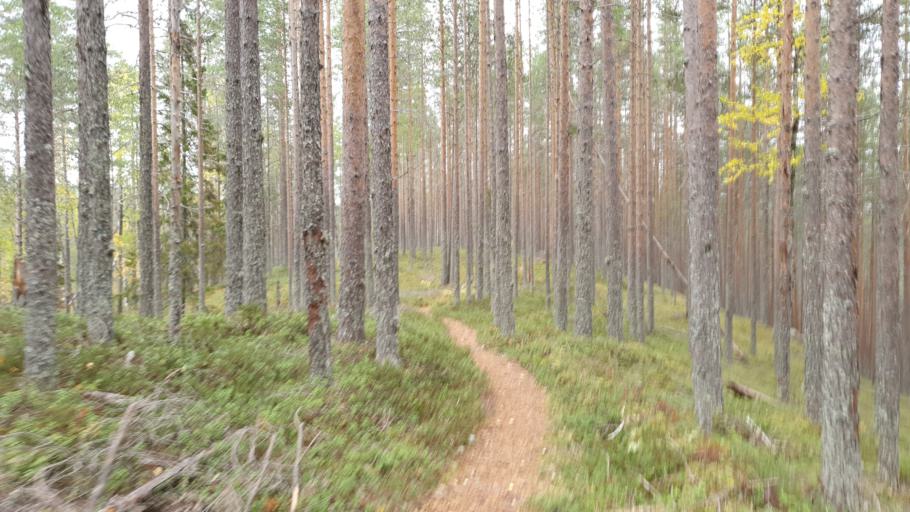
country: FI
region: Kainuu
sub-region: Kehys-Kainuu
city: Kuhmo
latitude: 64.2931
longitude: 29.3392
